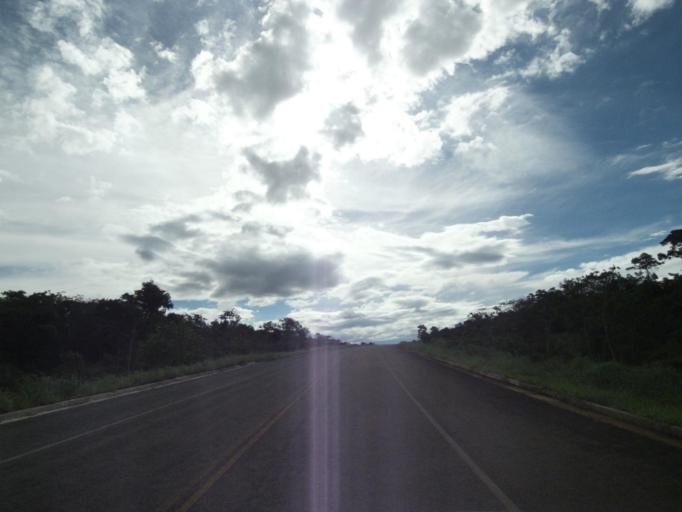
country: BR
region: Goias
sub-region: Jaragua
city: Jaragua
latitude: -15.8400
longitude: -49.2898
